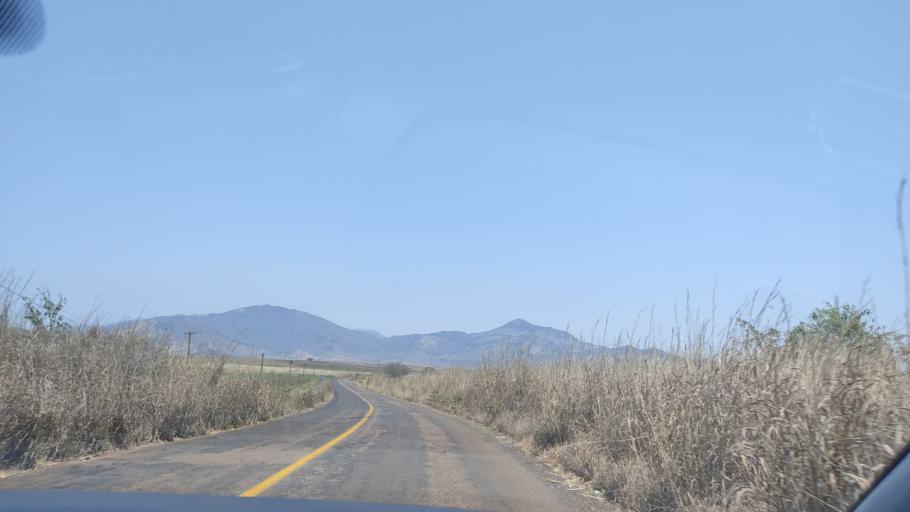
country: MX
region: Nayarit
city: Puga
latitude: 21.5773
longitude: -104.7548
